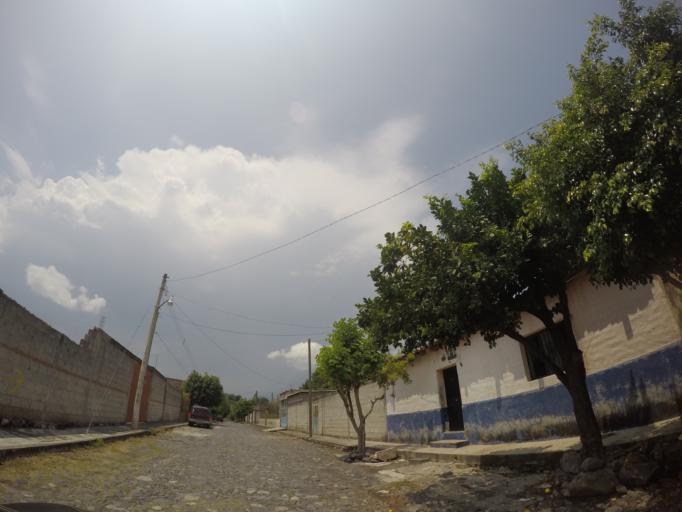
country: MX
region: Nayarit
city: Jala
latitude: 21.1059
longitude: -104.4356
